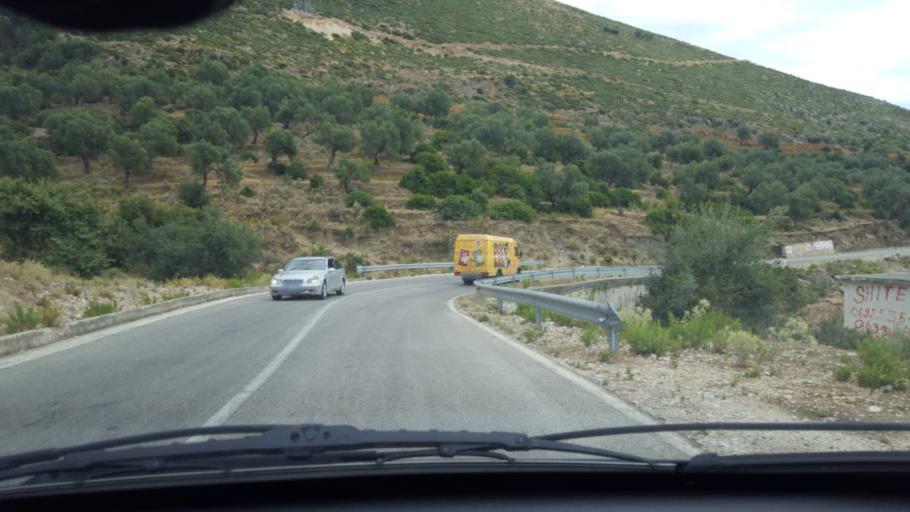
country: AL
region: Vlore
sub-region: Rrethi i Sarandes
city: Lukove
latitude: 40.0321
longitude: 19.8875
